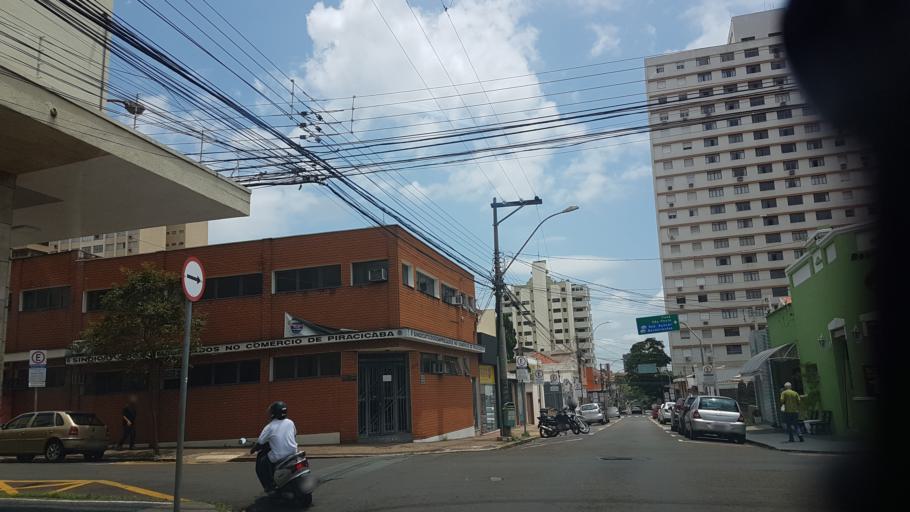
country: BR
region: Sao Paulo
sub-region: Piracicaba
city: Piracicaba
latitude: -22.7234
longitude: -47.6467
